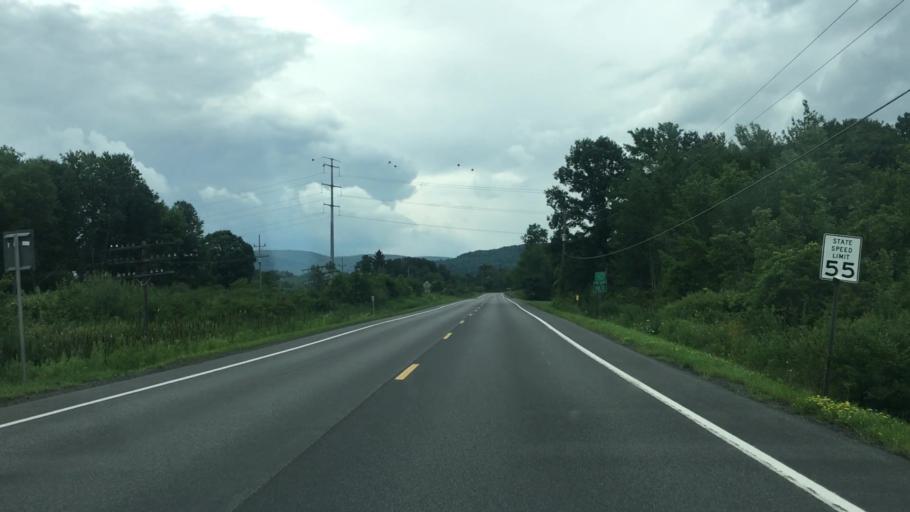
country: US
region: New York
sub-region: Otsego County
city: Otego
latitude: 42.4286
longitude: -75.1312
